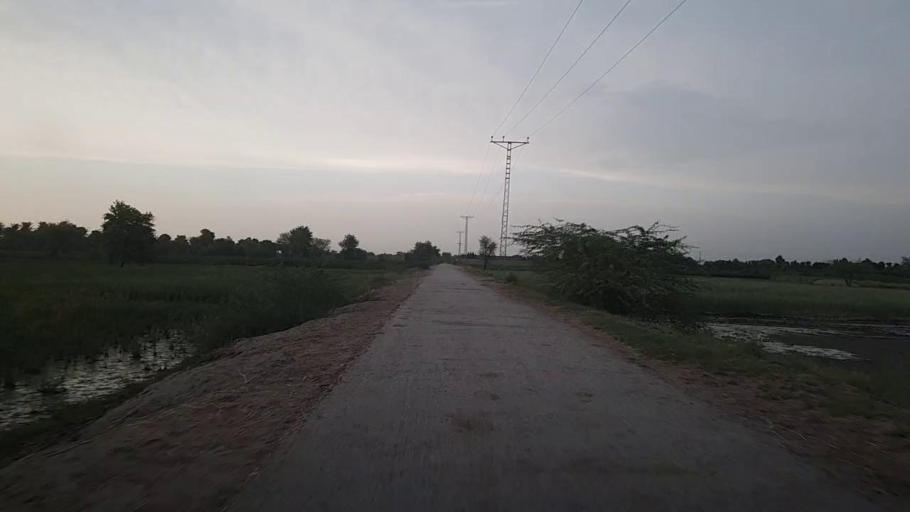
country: PK
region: Sindh
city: Karaundi
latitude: 27.0090
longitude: 68.3539
